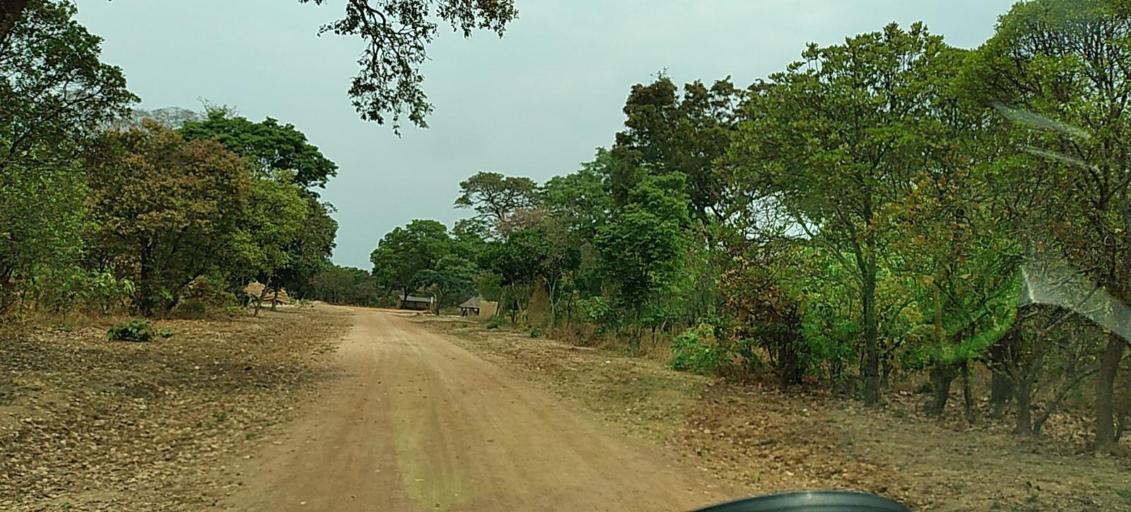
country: ZM
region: North-Western
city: Solwezi
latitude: -12.9649
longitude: 26.5706
